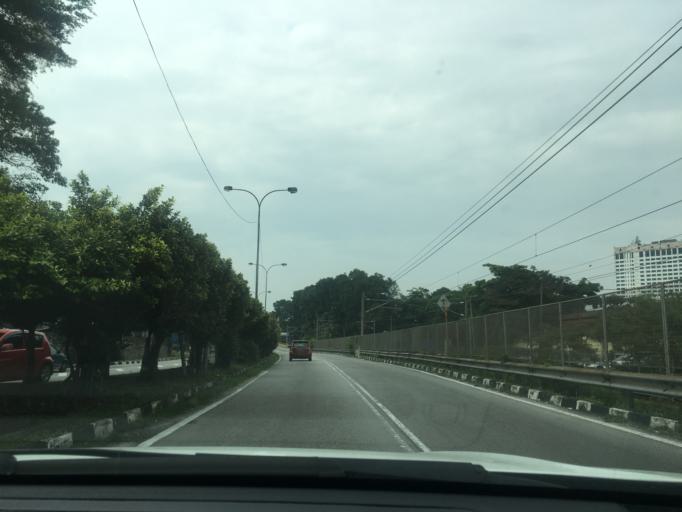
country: MY
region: Selangor
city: Klang
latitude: 3.0455
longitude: 101.4455
